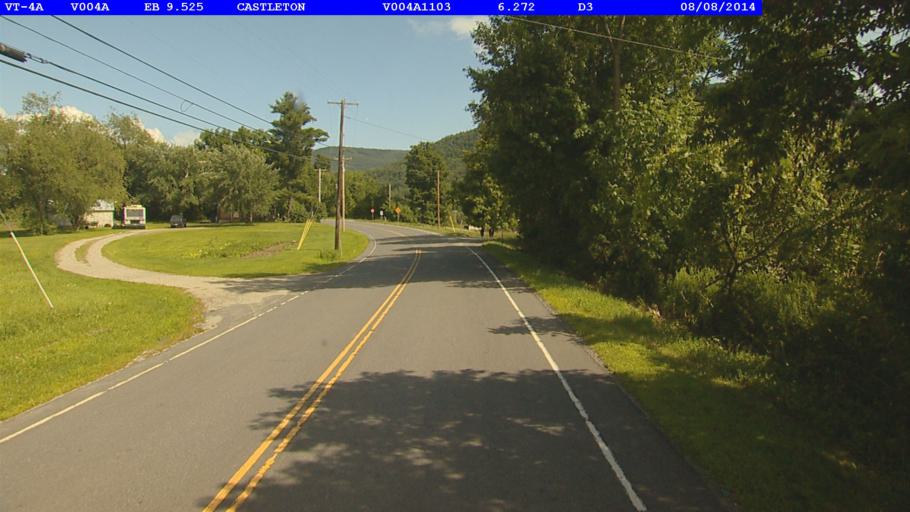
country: US
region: Vermont
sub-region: Rutland County
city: Castleton
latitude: 43.6107
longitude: -73.1254
